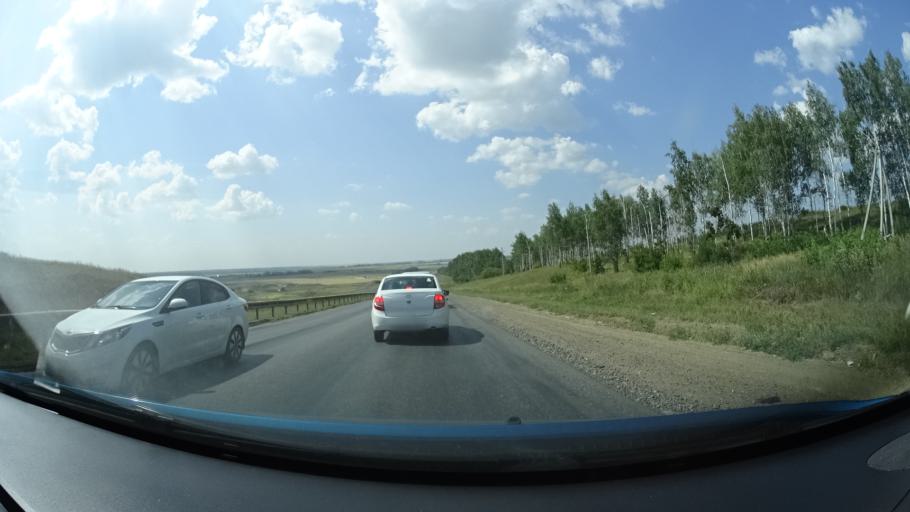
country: RU
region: Bashkortostan
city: Buzdyak
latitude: 54.6368
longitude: 54.4777
